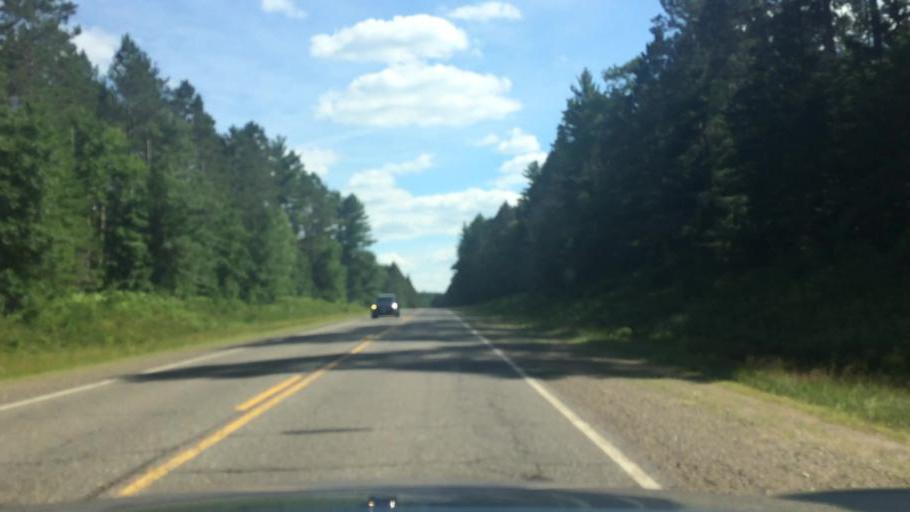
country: US
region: Wisconsin
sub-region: Vilas County
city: Lac du Flambeau
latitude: 46.0552
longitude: -89.6498
